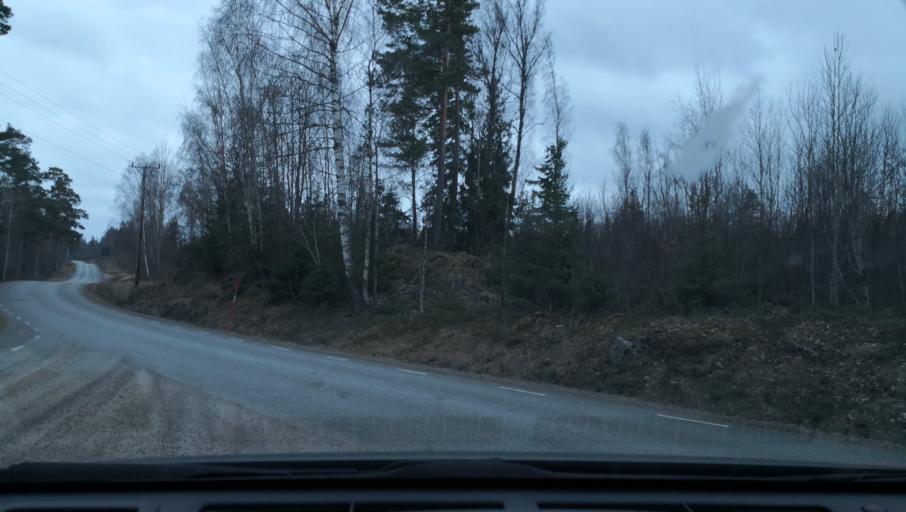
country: SE
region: OErebro
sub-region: Lindesbergs Kommun
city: Fellingsbro
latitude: 59.5750
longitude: 15.5667
